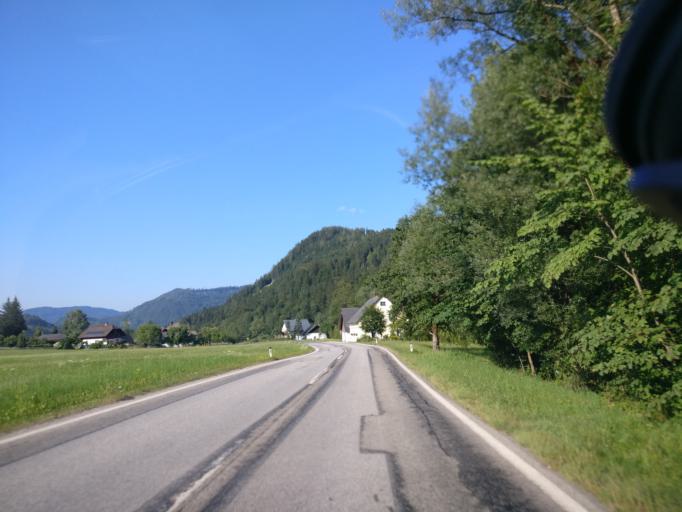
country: AT
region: Lower Austria
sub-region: Politischer Bezirk Scheibbs
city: Gostling an der Ybbs
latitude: 47.7824
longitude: 14.9130
